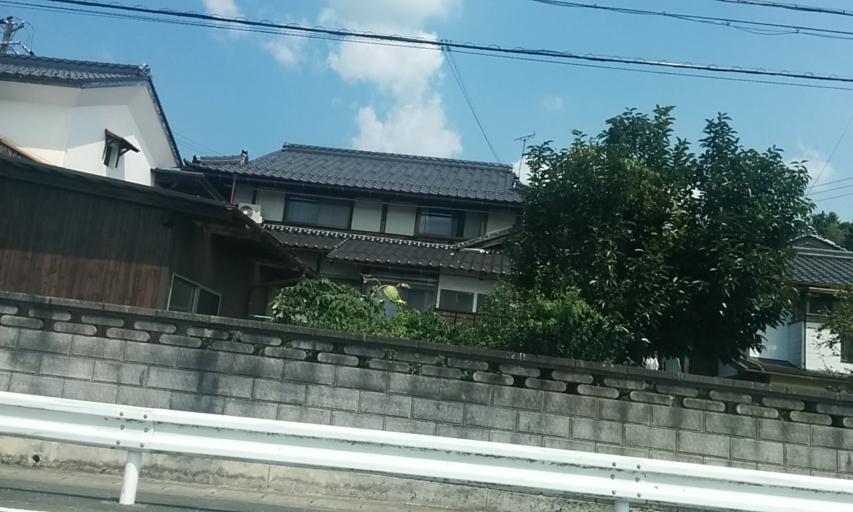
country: JP
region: Kyoto
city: Fukuchiyama
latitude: 35.3170
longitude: 135.1229
